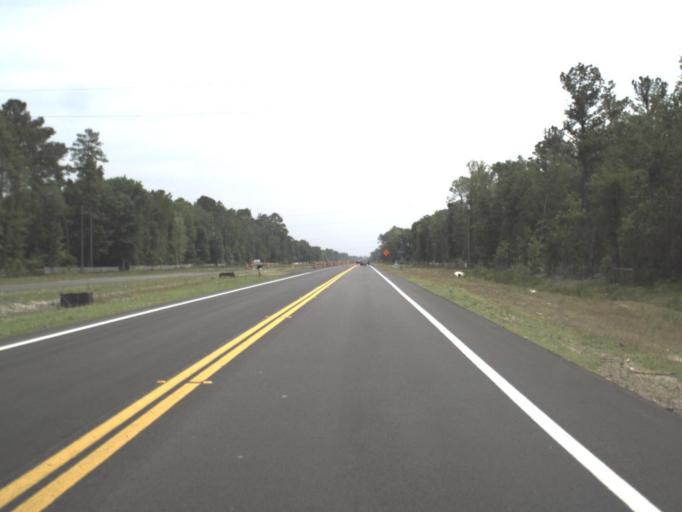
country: US
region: Florida
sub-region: Nassau County
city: Nassau Village-Ratliff
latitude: 30.4411
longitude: -81.9192
